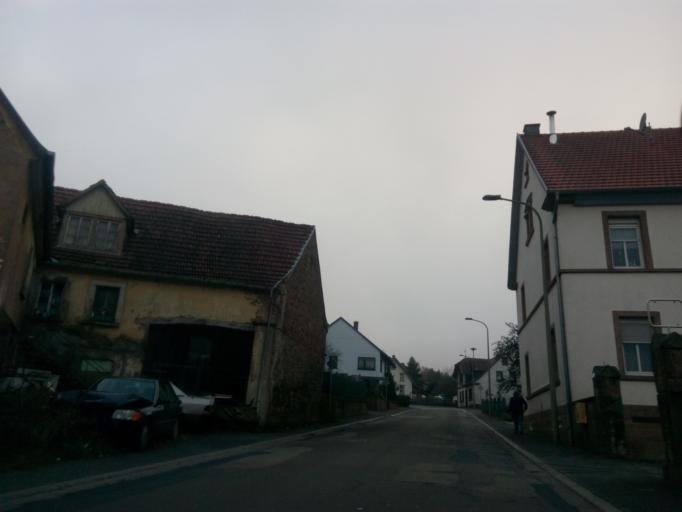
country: DE
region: Rheinland-Pfalz
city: Rothselberg
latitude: 49.5463
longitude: 7.5924
